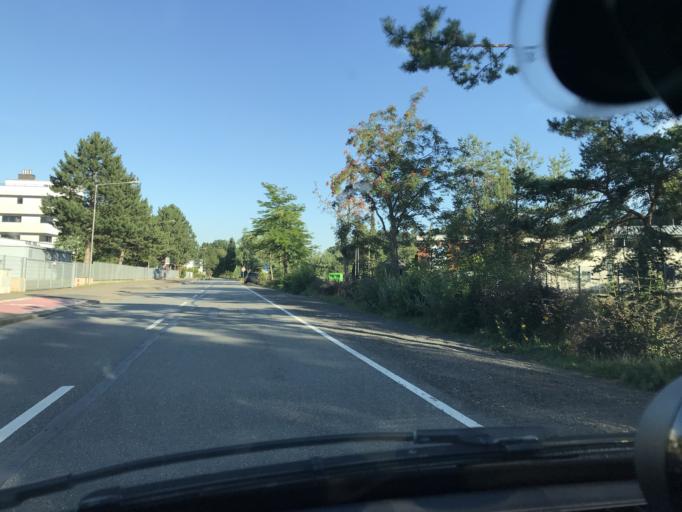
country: DE
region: Lower Saxony
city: Buxtehude
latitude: 53.4611
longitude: 9.7195
